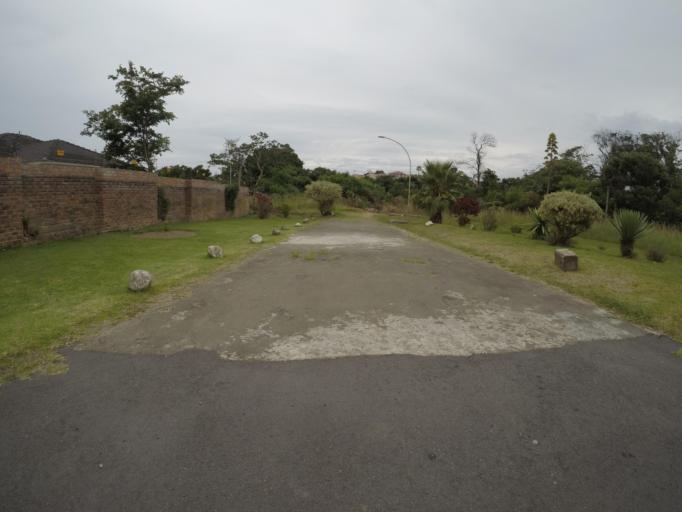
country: ZA
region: Eastern Cape
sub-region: Buffalo City Metropolitan Municipality
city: East London
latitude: -33.0005
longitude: 27.8552
